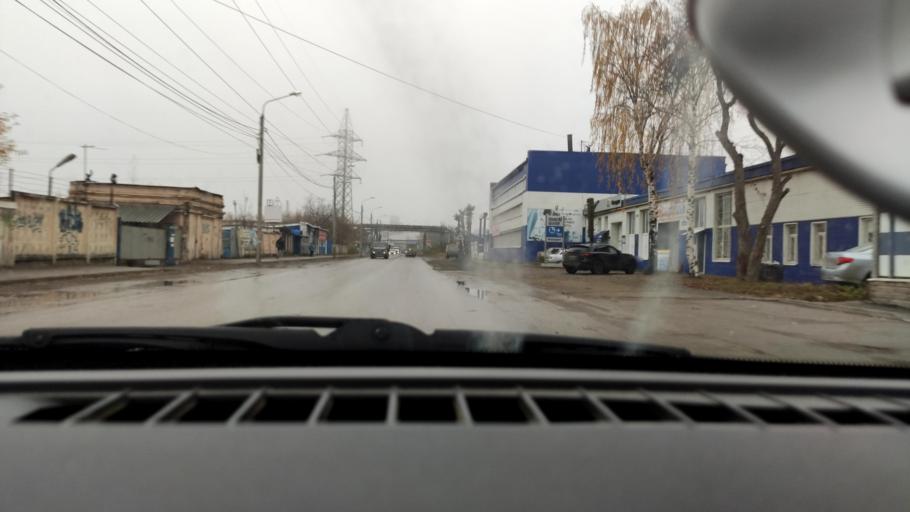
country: RU
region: Perm
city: Perm
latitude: 57.9672
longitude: 56.2577
